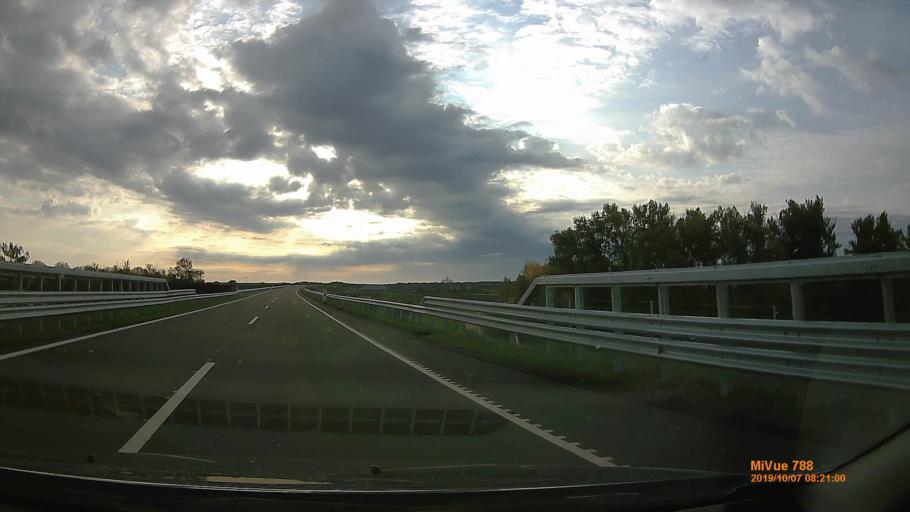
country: HU
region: Jasz-Nagykun-Szolnok
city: Kunszentmarton
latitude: 46.8639
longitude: 20.2913
